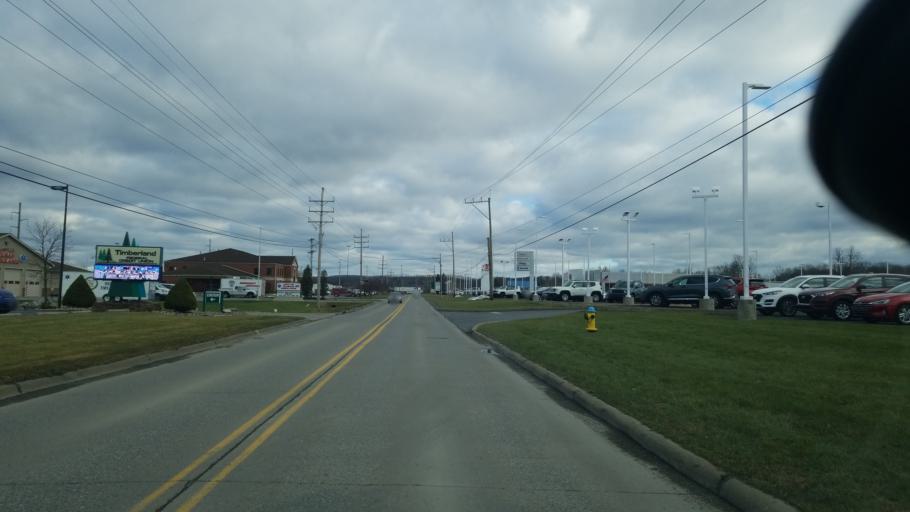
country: US
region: Pennsylvania
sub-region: Clearfield County
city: DuBois
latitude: 41.1211
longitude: -78.7401
